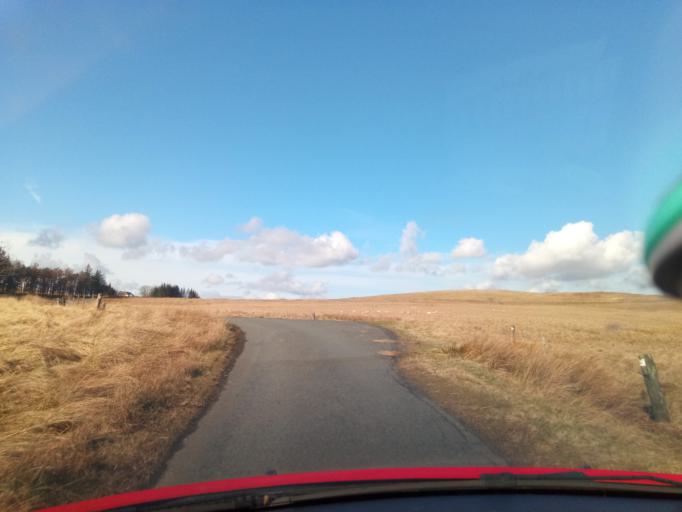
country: GB
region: Scotland
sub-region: The Scottish Borders
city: Hawick
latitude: 55.4388
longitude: -2.8786
